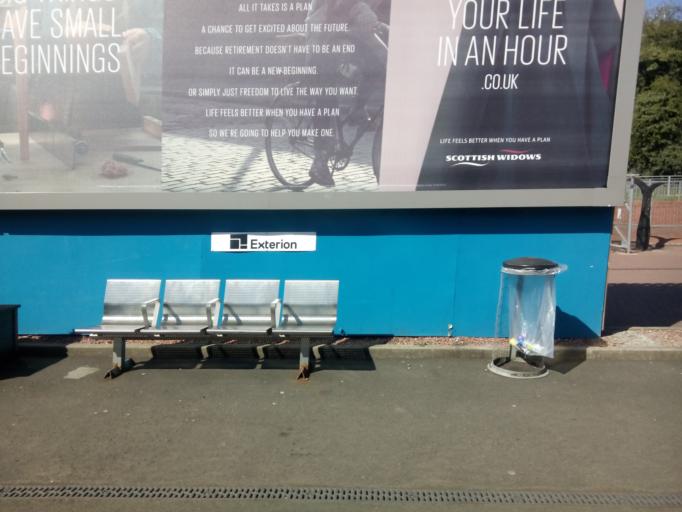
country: GB
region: Scotland
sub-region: Fife
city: Inverkeithing
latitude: 56.0349
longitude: -3.3955
